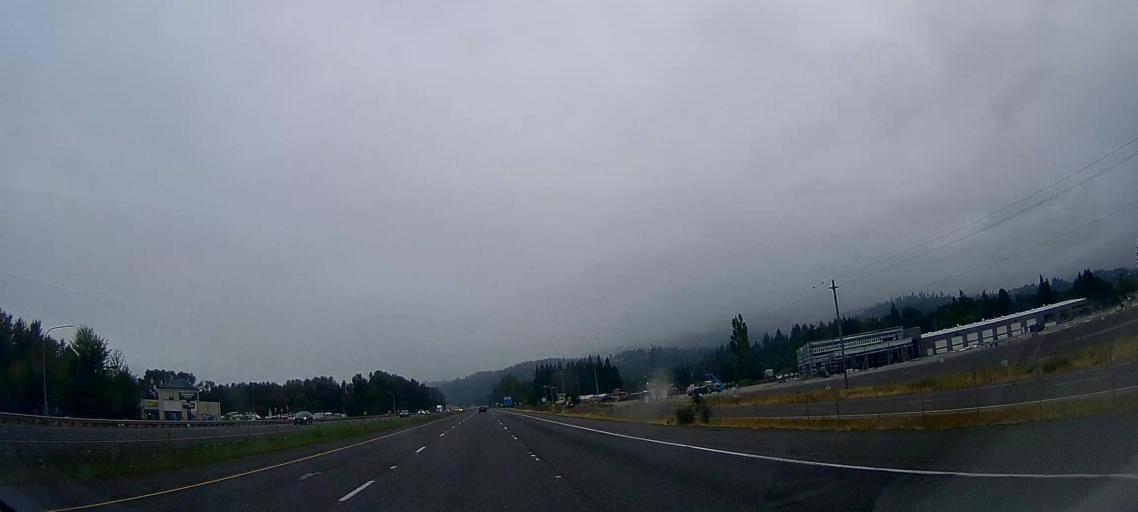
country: US
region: Washington
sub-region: Cowlitz County
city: Woodland
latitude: 45.9128
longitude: -122.7467
